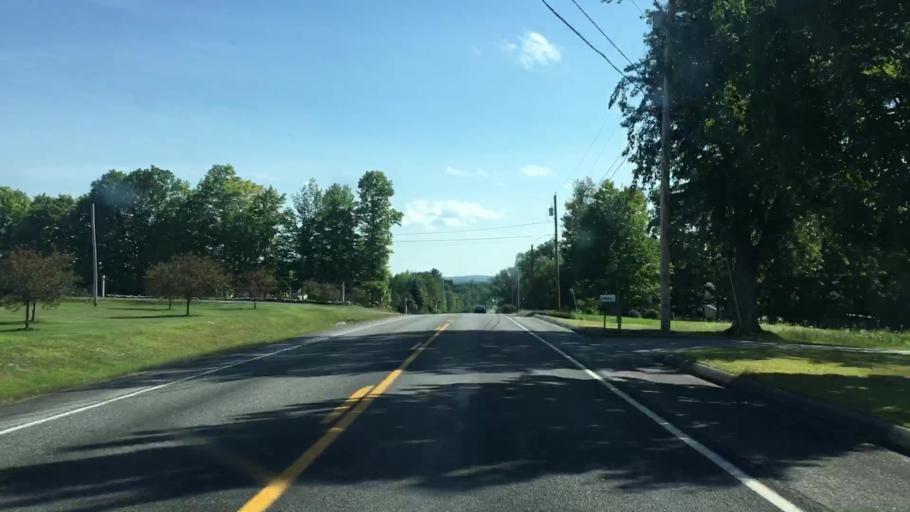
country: US
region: Maine
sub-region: Androscoggin County
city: Lisbon Falls
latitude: 44.0279
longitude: -70.0675
